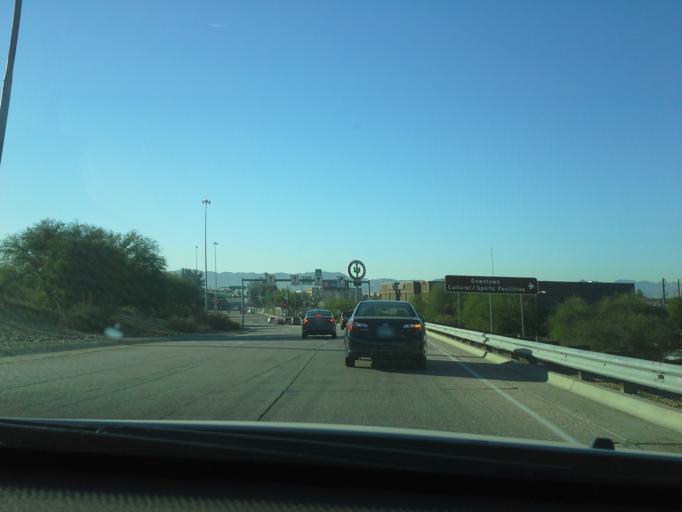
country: US
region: Arizona
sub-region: Maricopa County
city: Phoenix
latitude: 33.4502
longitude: -112.0378
